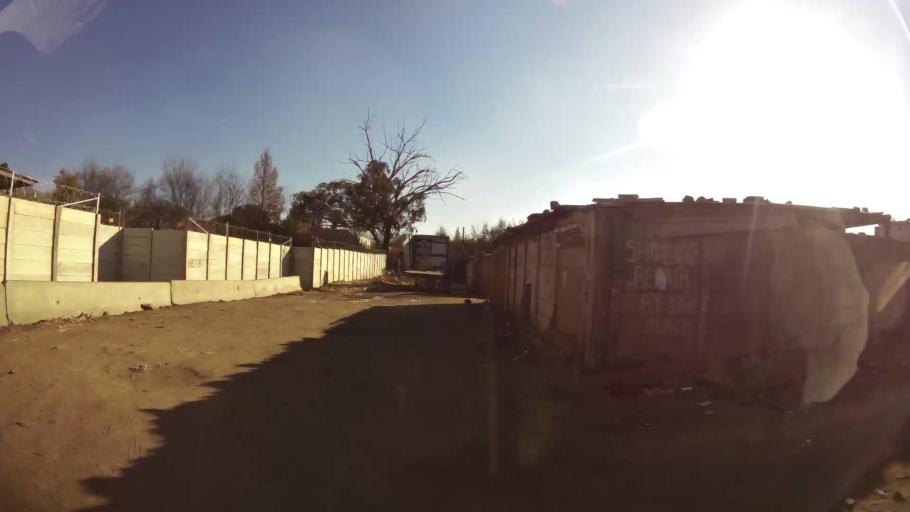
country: ZA
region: Gauteng
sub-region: City of Johannesburg Metropolitan Municipality
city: Johannesburg
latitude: -26.2079
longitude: 27.9917
